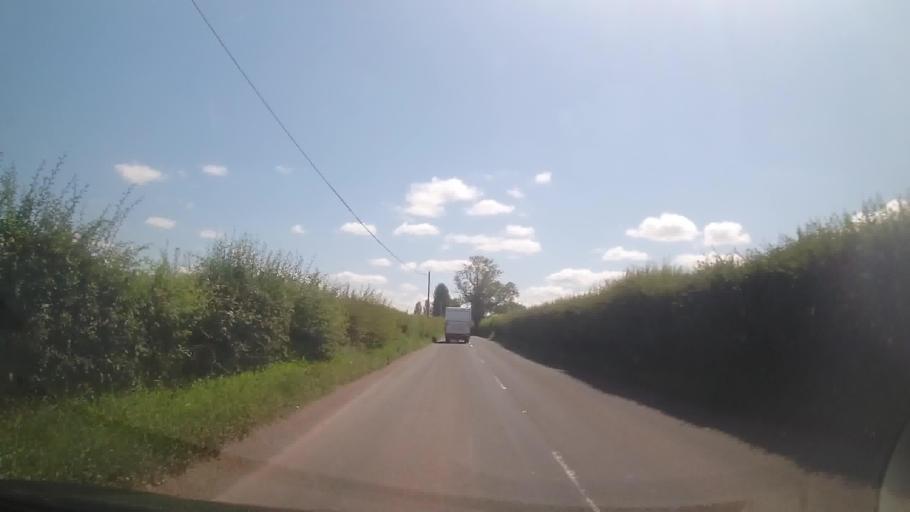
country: GB
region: England
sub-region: Herefordshire
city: Bodenham
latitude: 52.1538
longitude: -2.6518
